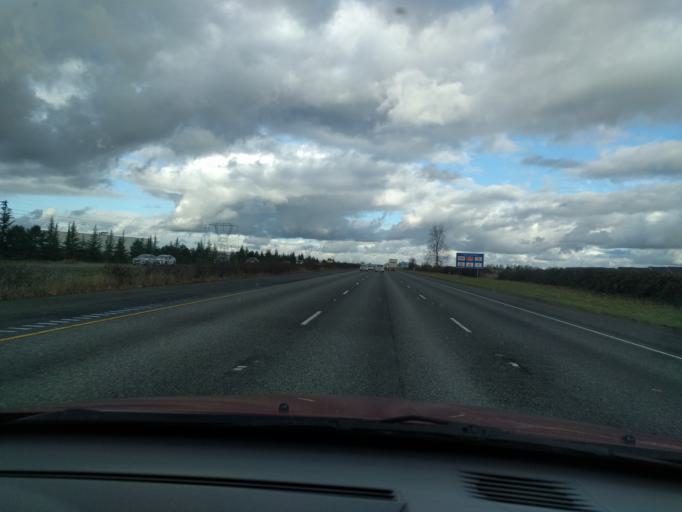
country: US
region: Oregon
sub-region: Marion County
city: Gervais
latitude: 45.1401
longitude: -122.8920
